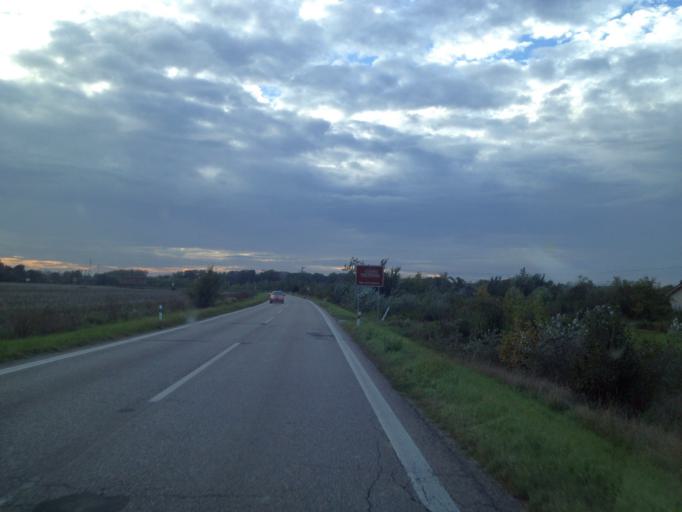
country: SK
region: Nitriansky
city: Komarno
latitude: 47.7662
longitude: 18.1598
